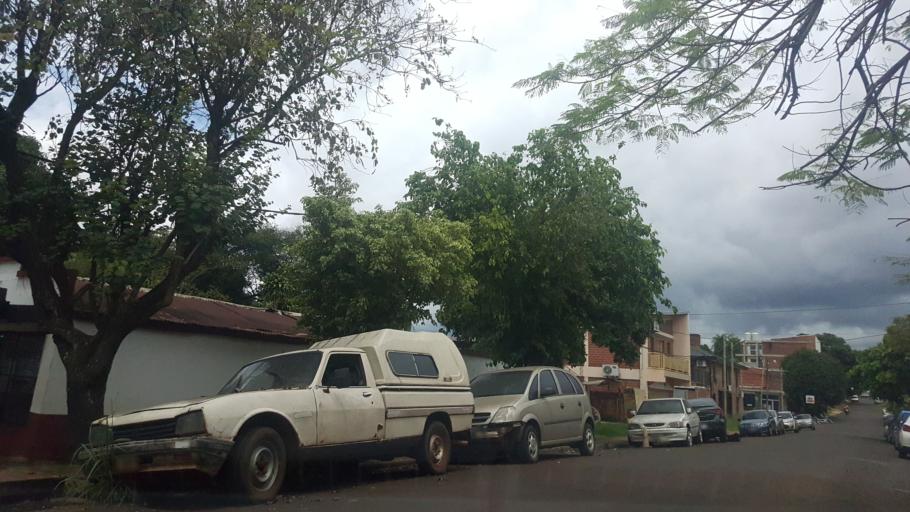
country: AR
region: Misiones
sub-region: Departamento de Capital
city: Posadas
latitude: -27.3696
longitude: -55.9112
